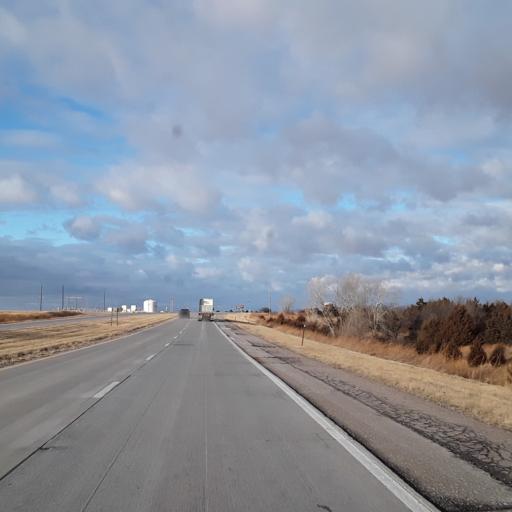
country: US
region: Nebraska
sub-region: Thayer County
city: Hebron
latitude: 40.1815
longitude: -97.5750
